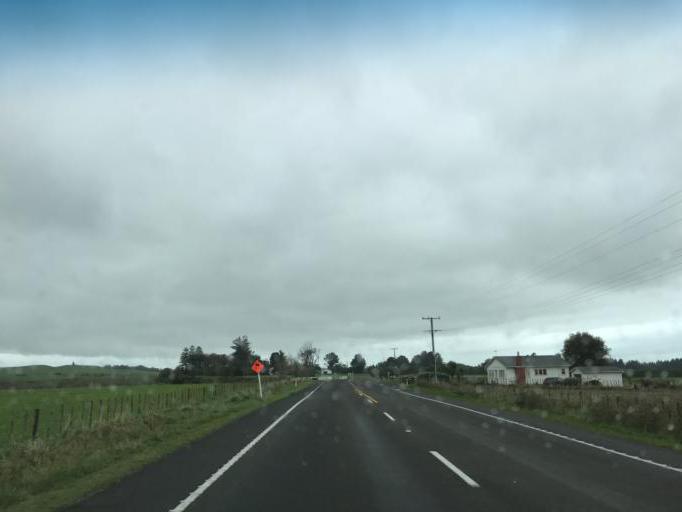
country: NZ
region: Manawatu-Wanganui
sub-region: Wanganui District
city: Wanganui
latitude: -39.8176
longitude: 174.8317
